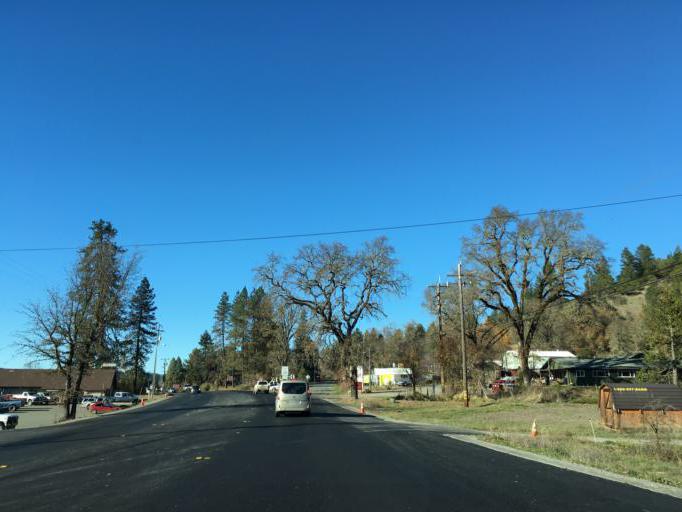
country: US
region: California
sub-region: Mendocino County
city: Laytonville
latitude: 39.6834
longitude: -123.4777
